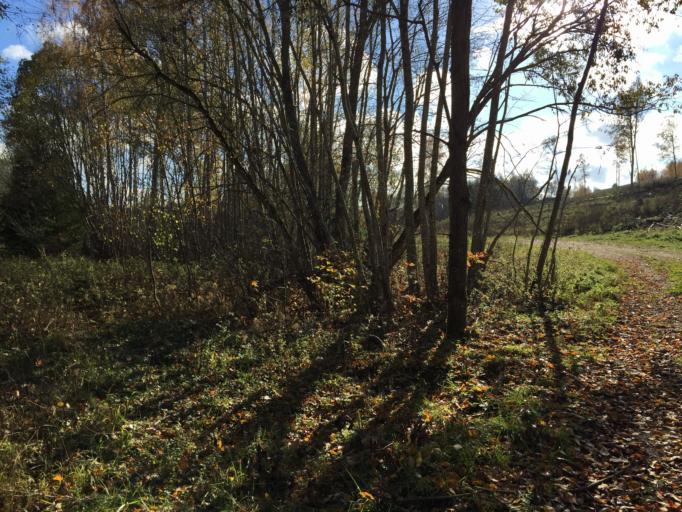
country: LV
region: Tukuma Rajons
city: Tukums
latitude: 56.9664
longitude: 22.9889
